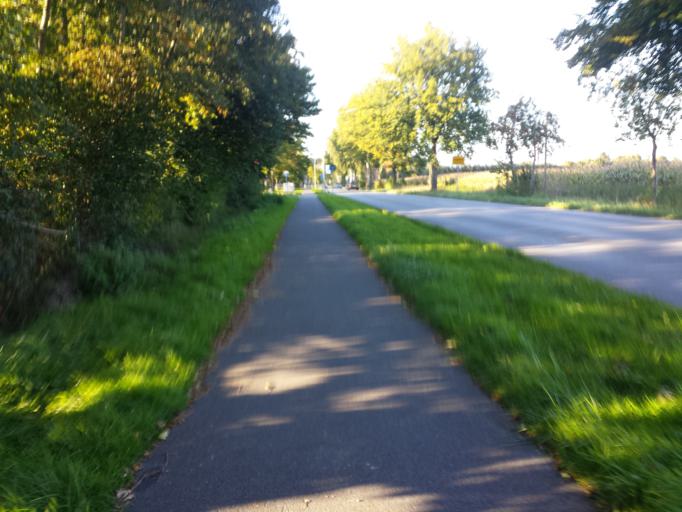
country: DE
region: North Rhine-Westphalia
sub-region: Regierungsbezirk Detmold
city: Langenberg
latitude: 51.7617
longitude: 8.3217
